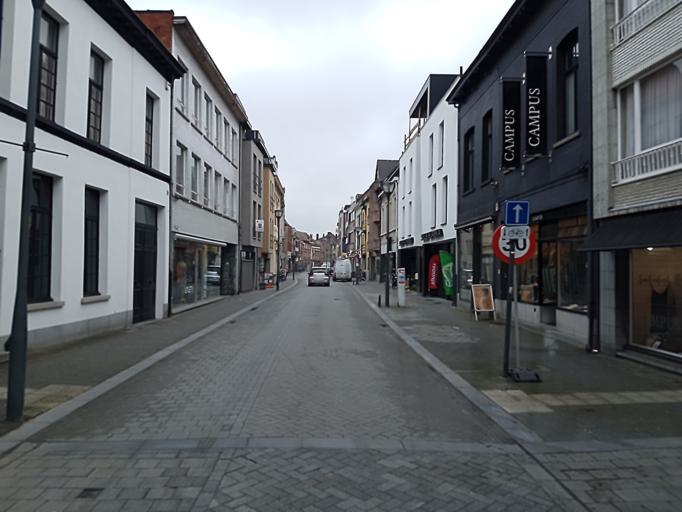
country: BE
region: Flanders
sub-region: Provincie Antwerpen
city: Turnhout
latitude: 51.3255
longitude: 4.9496
